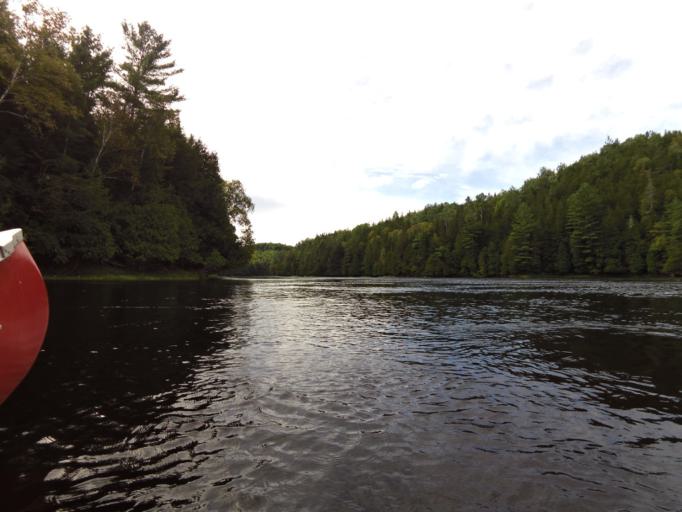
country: CA
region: Quebec
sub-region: Outaouais
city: Wakefield
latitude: 45.7993
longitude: -75.9314
